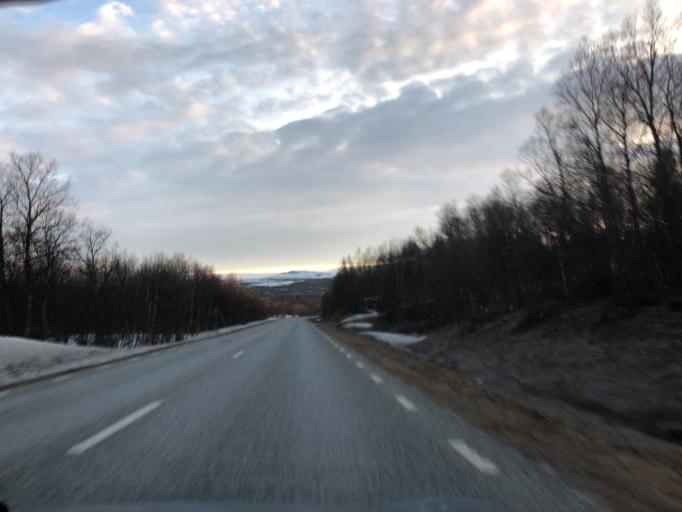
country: NO
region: Hedmark
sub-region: Engerdal
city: Engerdal
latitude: 62.5347
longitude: 12.3847
